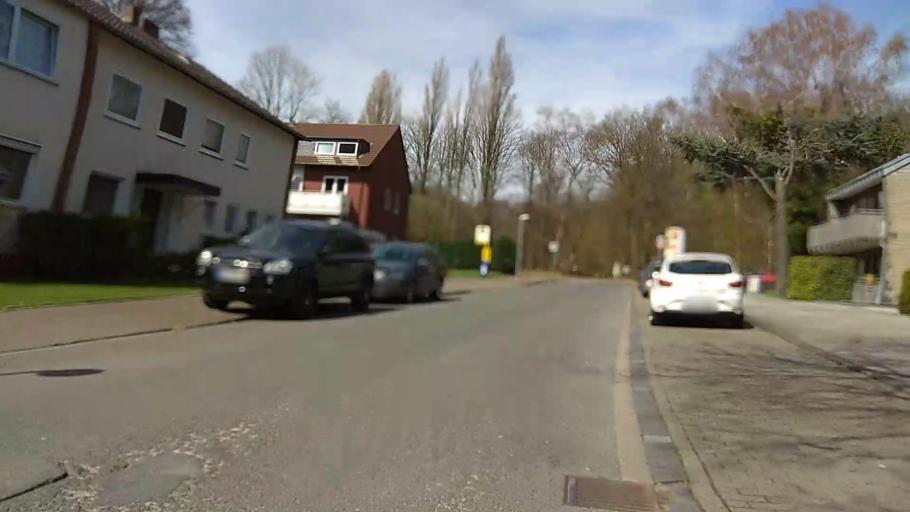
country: DE
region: North Rhine-Westphalia
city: Herten
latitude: 51.5793
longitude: 7.0705
